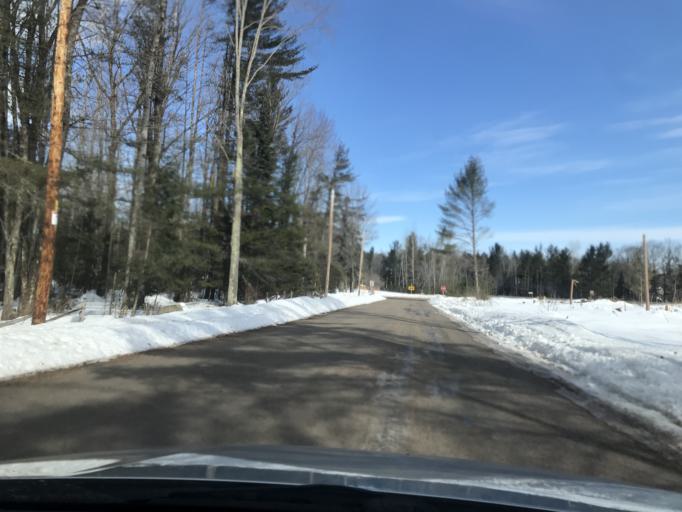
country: US
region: Wisconsin
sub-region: Oconto County
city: Gillett
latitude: 45.1242
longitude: -88.4194
